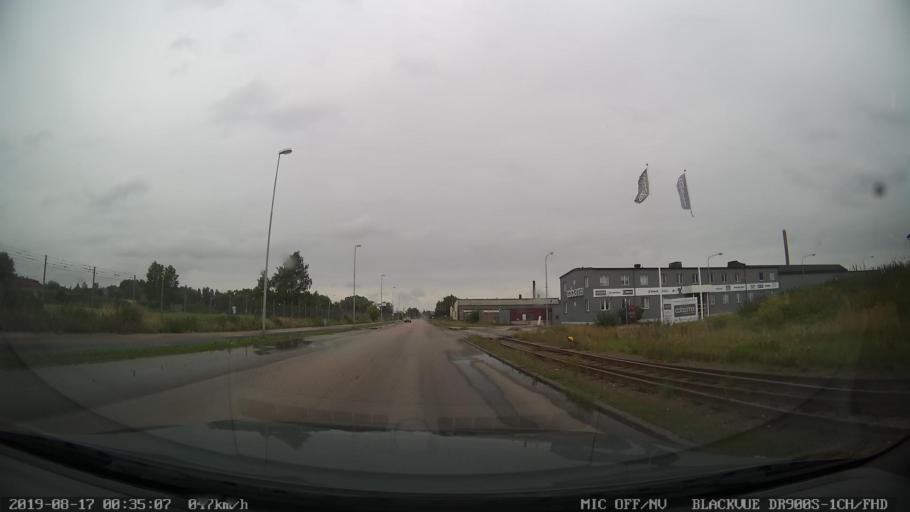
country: SE
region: Skane
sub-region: Landskrona
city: Landskrona
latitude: 55.8638
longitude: 12.8376
